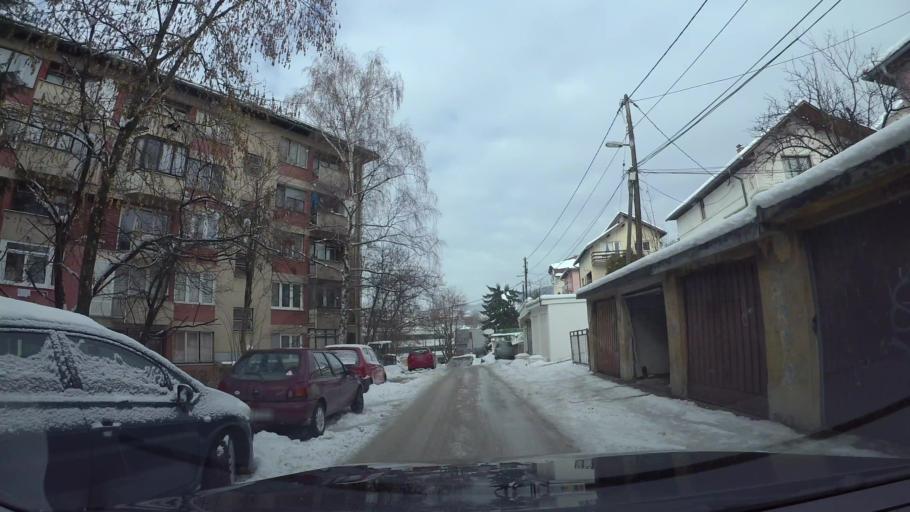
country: BA
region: Federation of Bosnia and Herzegovina
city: Kobilja Glava
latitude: 43.8750
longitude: 18.4132
